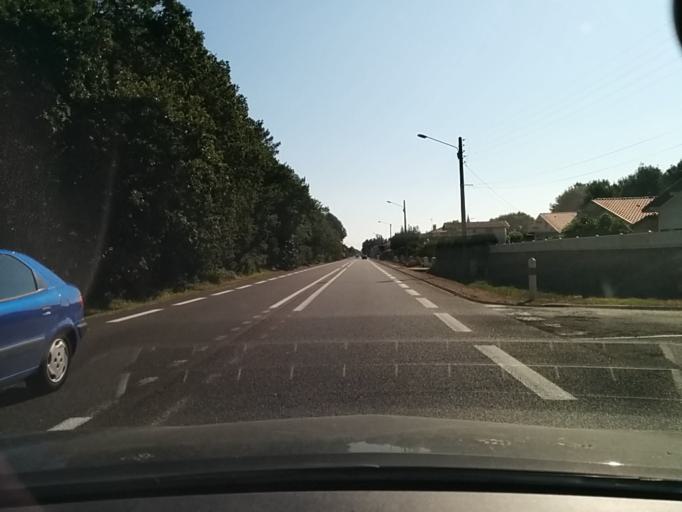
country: FR
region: Aquitaine
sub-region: Departement des Landes
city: Benesse-Maremne
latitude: 43.6352
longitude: -1.3563
